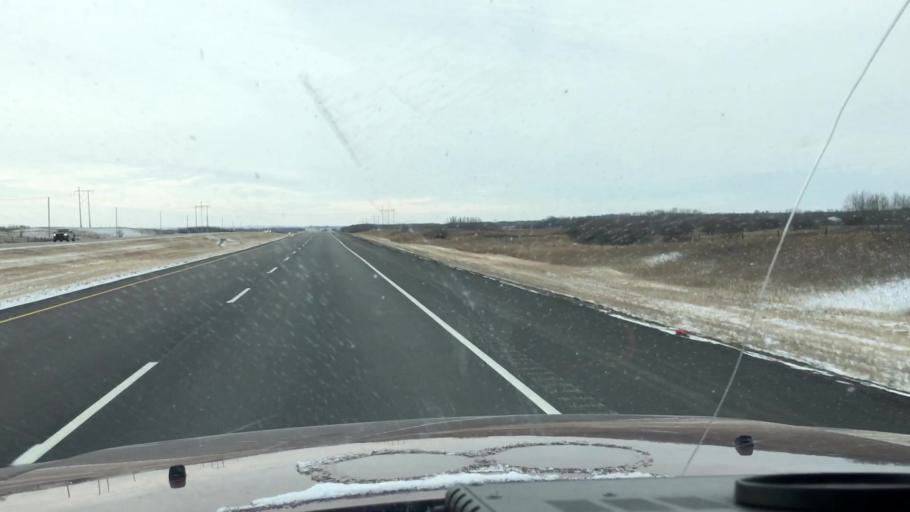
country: CA
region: Saskatchewan
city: Saskatoon
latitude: 51.8962
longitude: -106.5196
